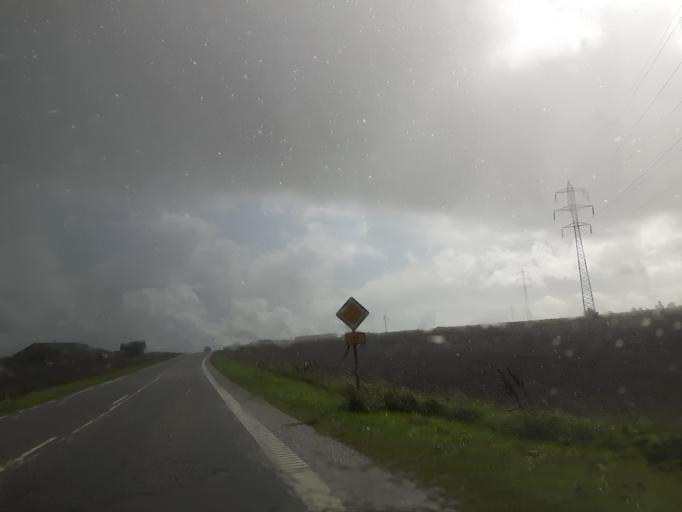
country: DK
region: Central Jutland
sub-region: Struer Kommune
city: Struer
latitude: 56.6222
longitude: 8.5186
